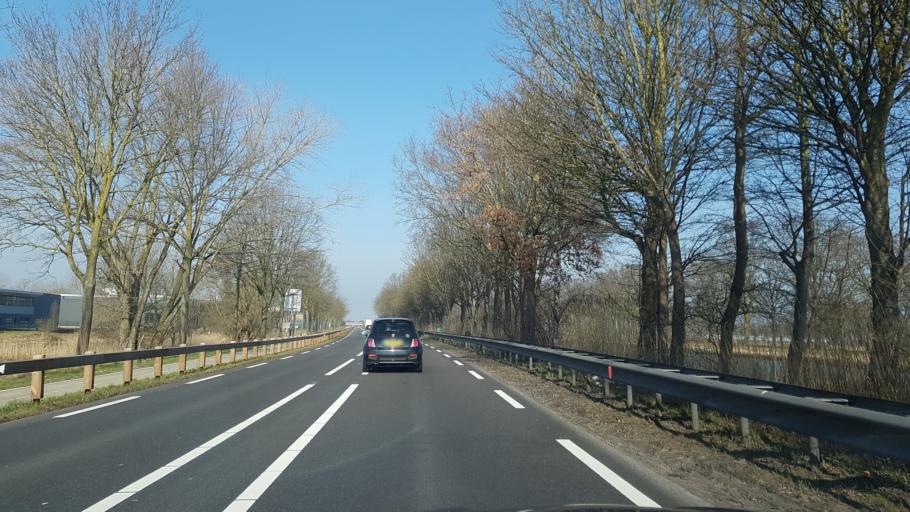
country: NL
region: North Brabant
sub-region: Gemeente Asten
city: Asten
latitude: 51.3913
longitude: 5.7337
